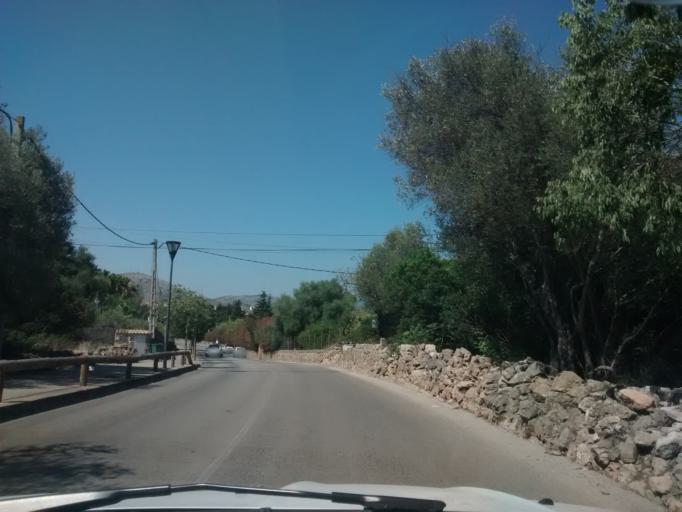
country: ES
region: Balearic Islands
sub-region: Illes Balears
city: Alcudia
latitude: 39.8559
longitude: 3.1333
